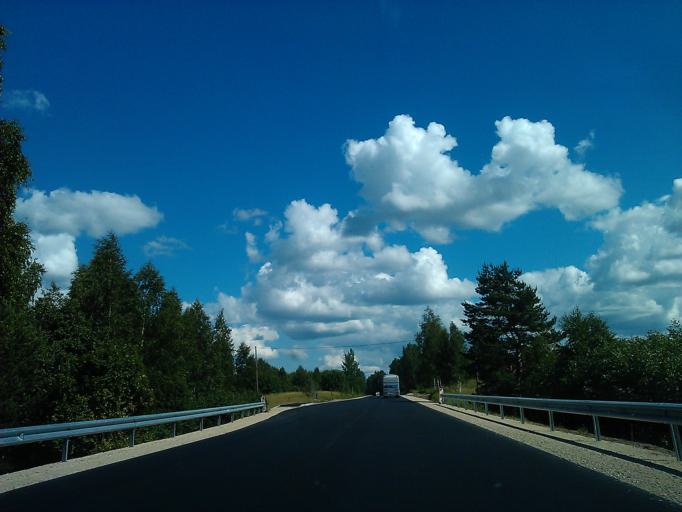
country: LV
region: Vilanu
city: Vilani
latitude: 56.5512
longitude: 27.0962
